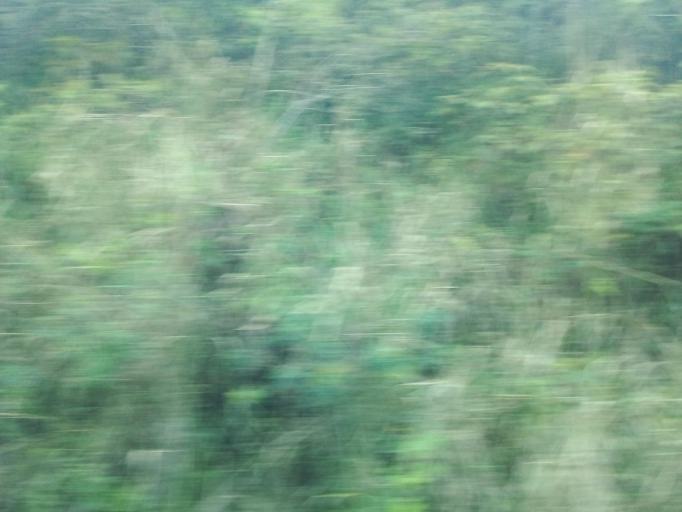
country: BR
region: Minas Gerais
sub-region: Rio Piracicaba
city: Rio Piracicaba
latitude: -19.9729
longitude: -43.2100
